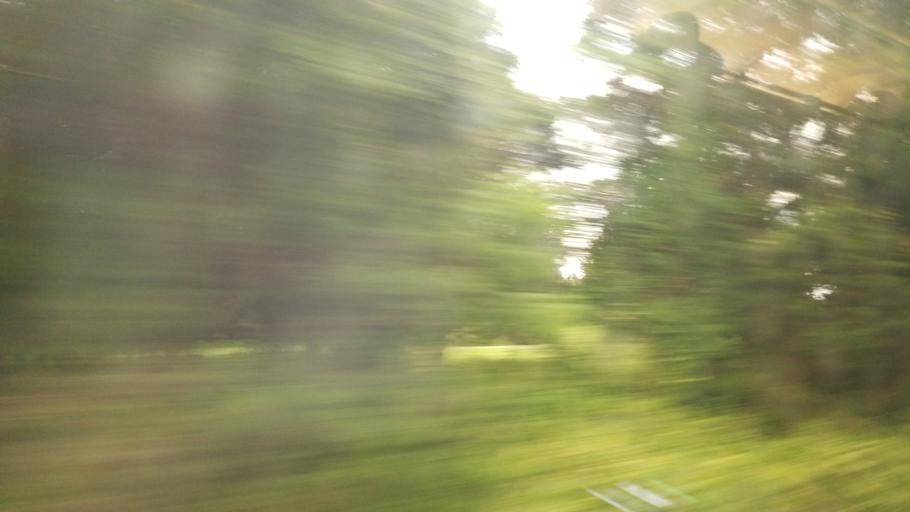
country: US
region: Virginia
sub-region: Prince William County
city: Nokesville
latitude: 38.6584
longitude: -77.6328
